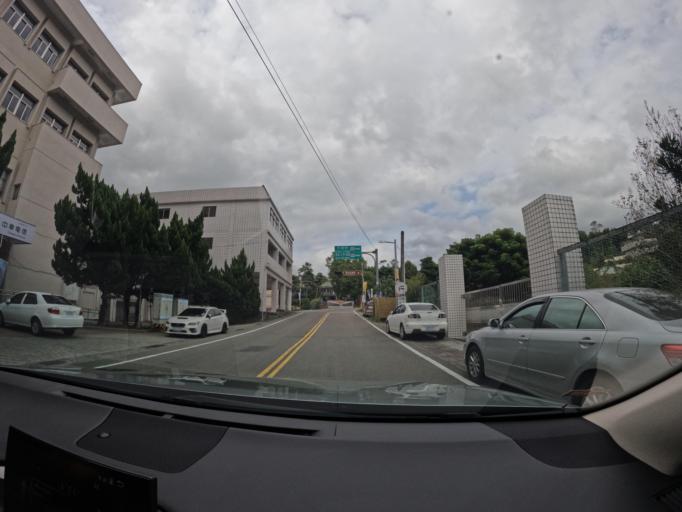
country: TW
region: Taiwan
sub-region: Miaoli
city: Miaoli
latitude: 24.4258
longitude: 120.8705
